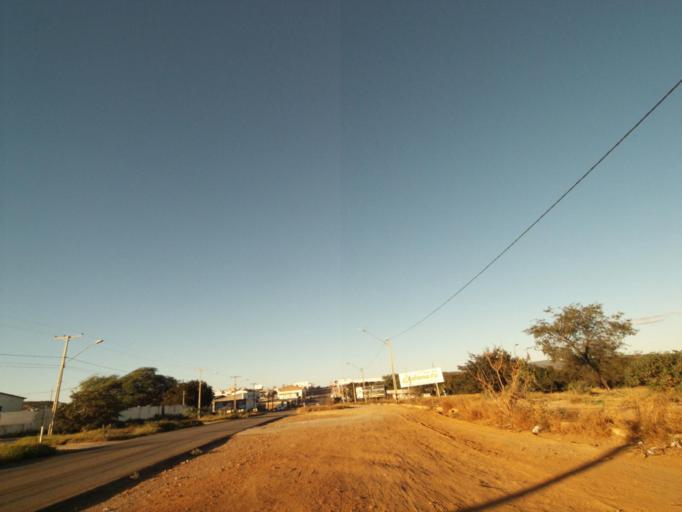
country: BR
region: Bahia
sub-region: Brumado
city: Brumado
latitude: -14.2200
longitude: -41.6888
